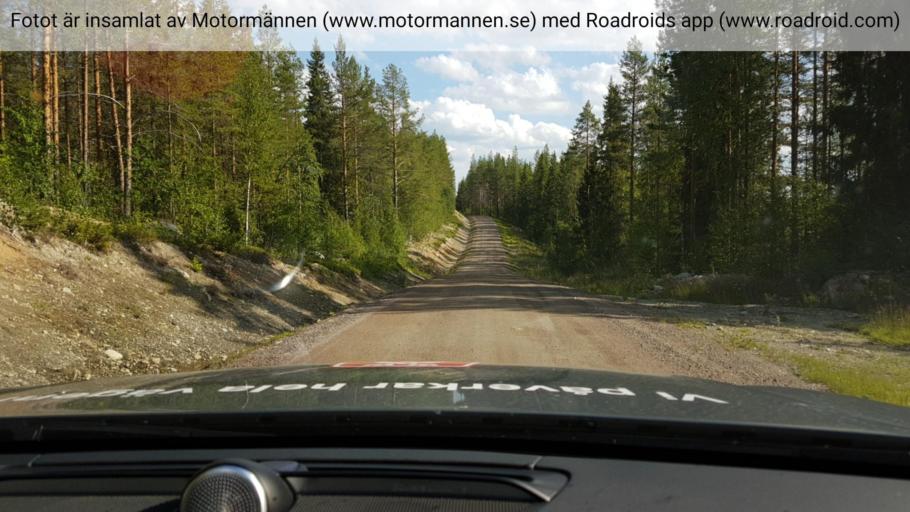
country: SE
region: Vaesterbotten
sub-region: Dorotea Kommun
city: Dorotea
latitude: 63.9693
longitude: 16.0672
